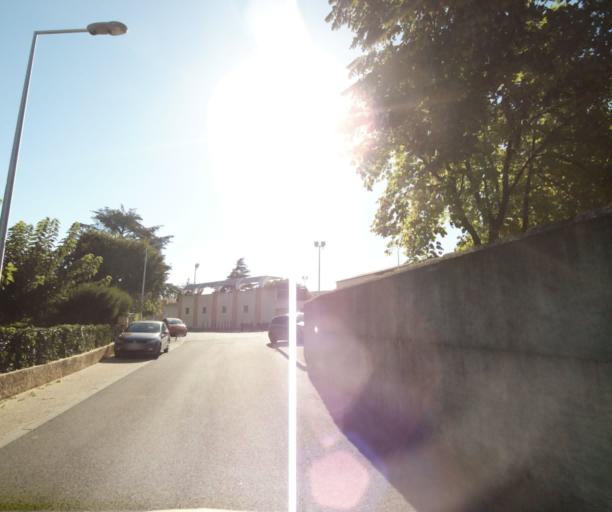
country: FR
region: Languedoc-Roussillon
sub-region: Departement du Gard
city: Bouillargues
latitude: 43.7992
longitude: 4.4229
